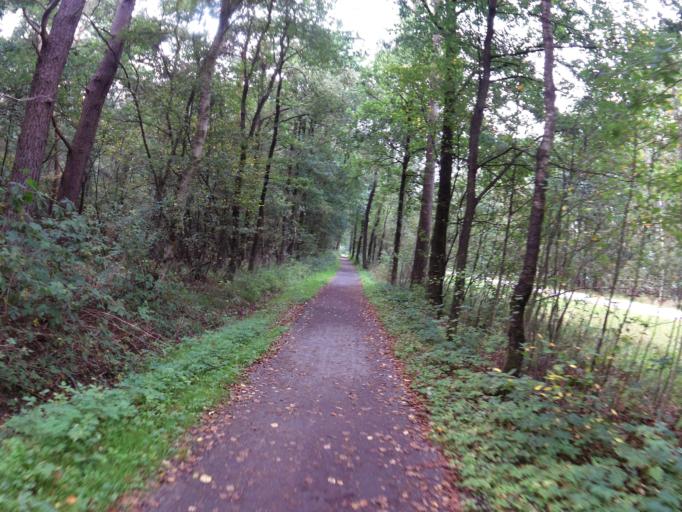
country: NL
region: Drenthe
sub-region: Gemeente Westerveld
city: Dwingeloo
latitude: 52.8162
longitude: 6.3740
